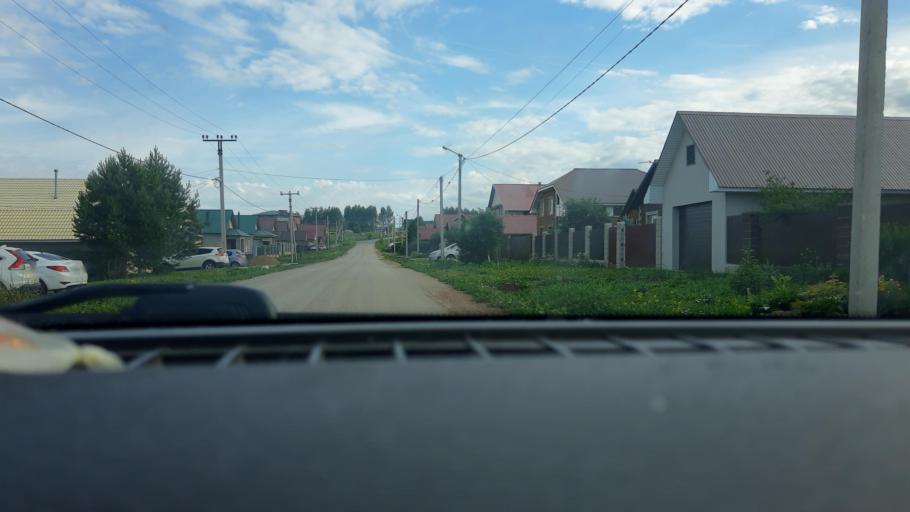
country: RU
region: Bashkortostan
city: Kabakovo
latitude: 54.6645
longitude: 56.2155
